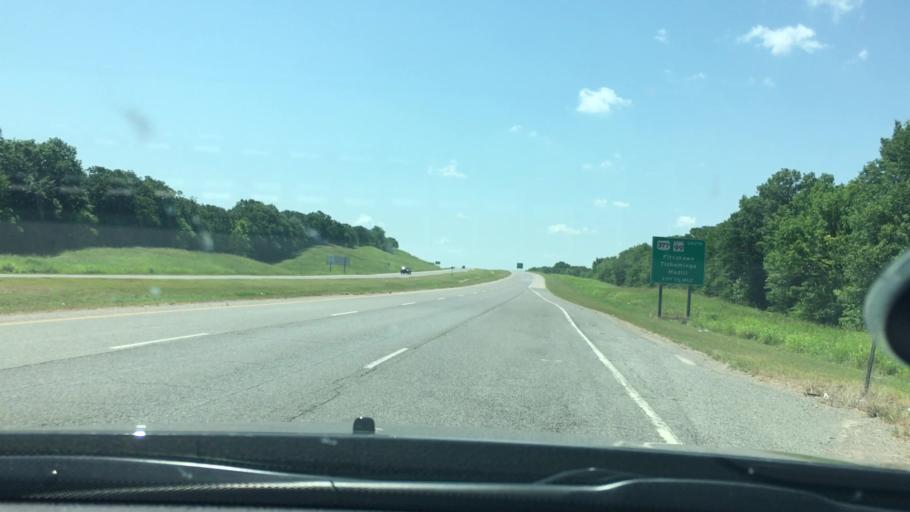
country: US
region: Oklahoma
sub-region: Pontotoc County
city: Ada
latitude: 34.7354
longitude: -96.6431
